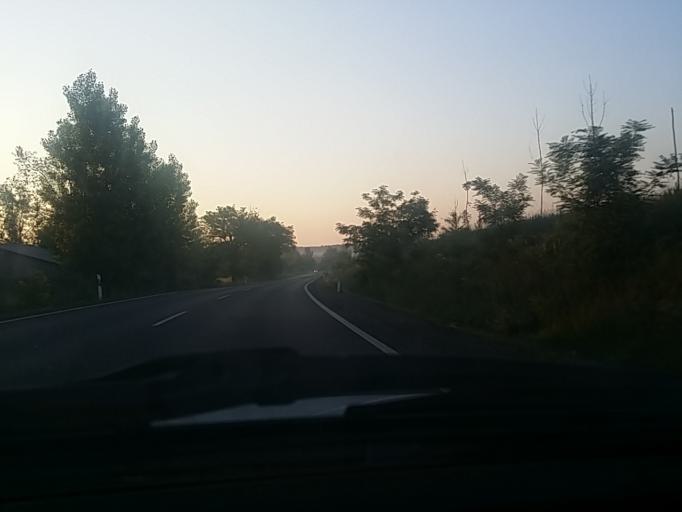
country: HU
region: Pest
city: Maglod
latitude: 47.4472
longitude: 19.3833
